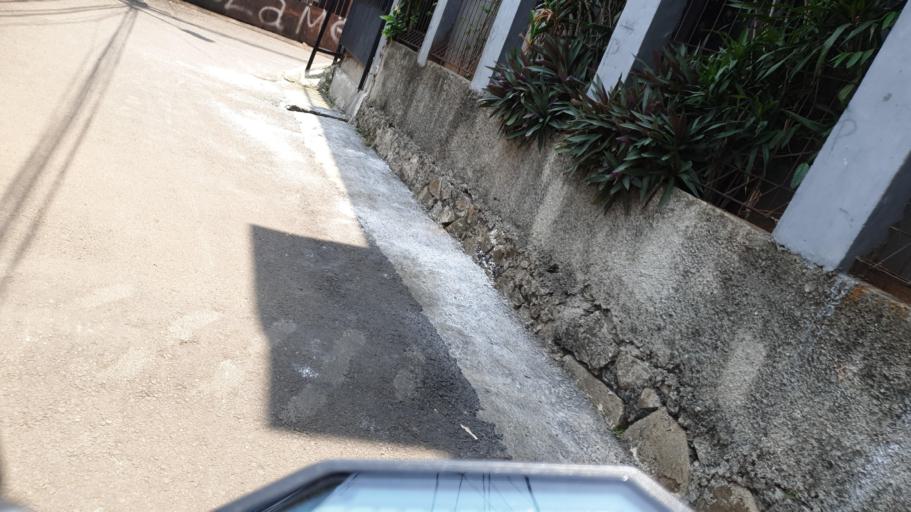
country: ID
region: West Java
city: Depok
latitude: -6.3276
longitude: 106.8321
